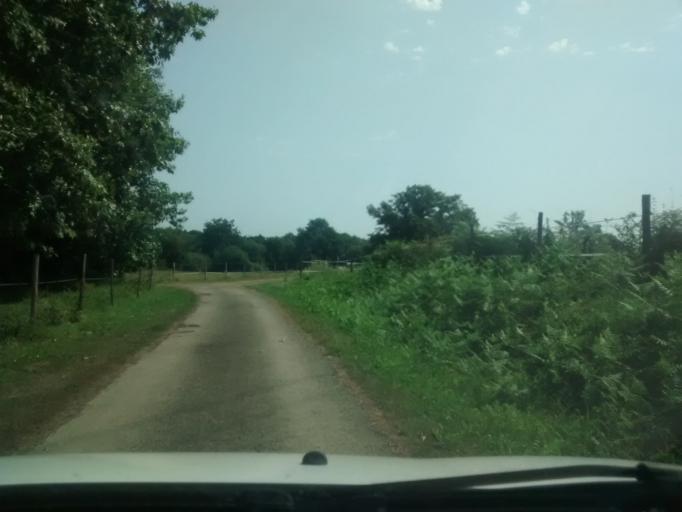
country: FR
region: Brittany
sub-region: Departement d'Ille-et-Vilaine
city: Fouillard
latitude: 48.1423
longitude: -1.5921
